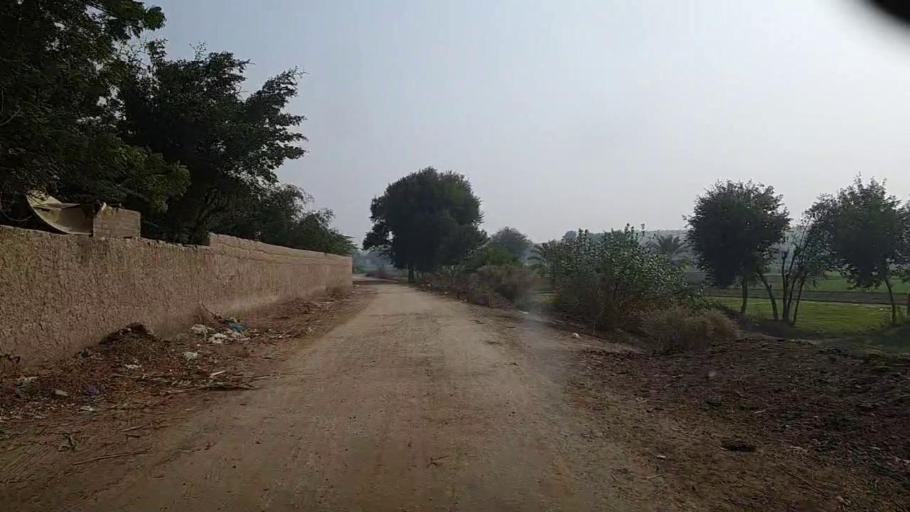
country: PK
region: Sindh
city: Bozdar
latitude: 27.0592
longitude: 68.6531
